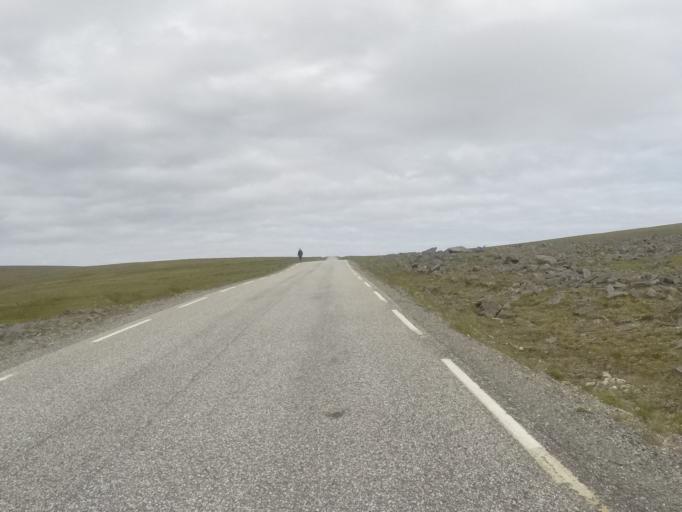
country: NO
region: Finnmark Fylke
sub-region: Nordkapp
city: Honningsvag
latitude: 71.1449
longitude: 25.7649
